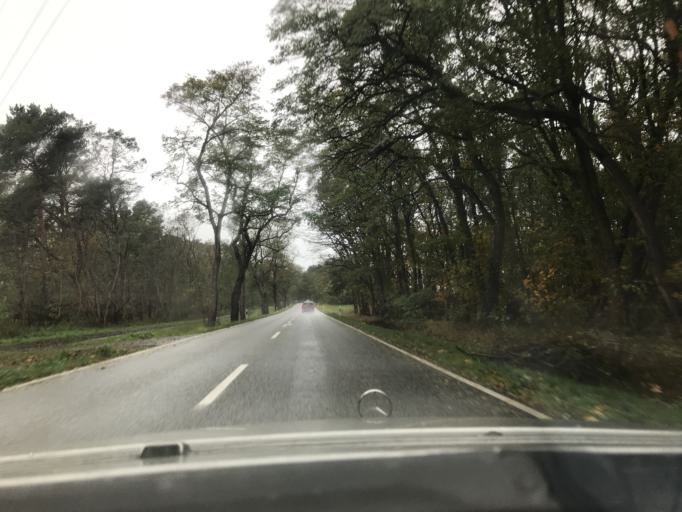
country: DE
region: Brandenburg
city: Trebbin
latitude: 52.2114
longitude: 13.1262
